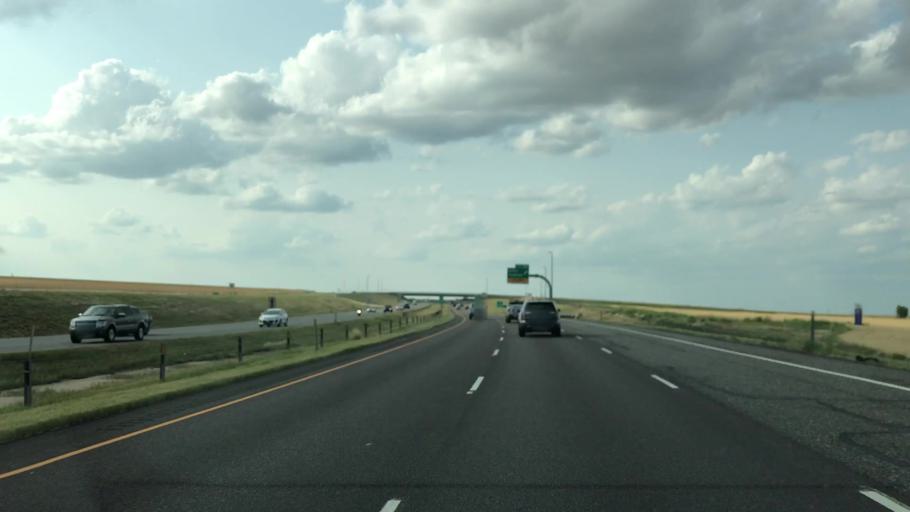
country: US
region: Colorado
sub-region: Adams County
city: Aurora
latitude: 39.8063
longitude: -104.7169
